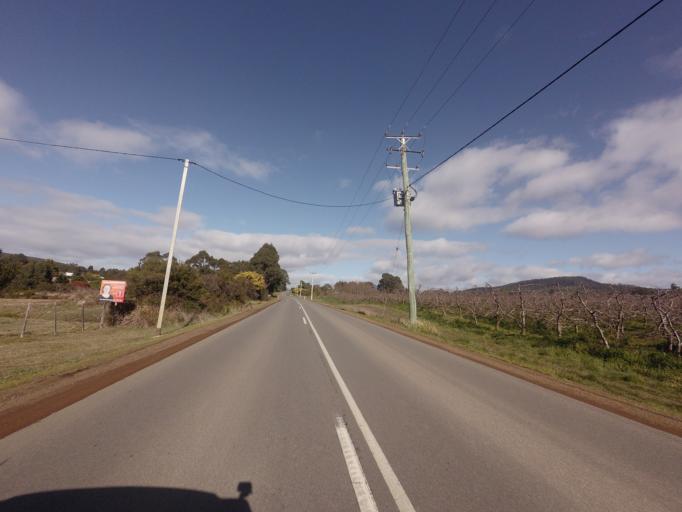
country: AU
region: Tasmania
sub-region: Huon Valley
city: Geeveston
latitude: -43.3235
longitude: 146.9959
